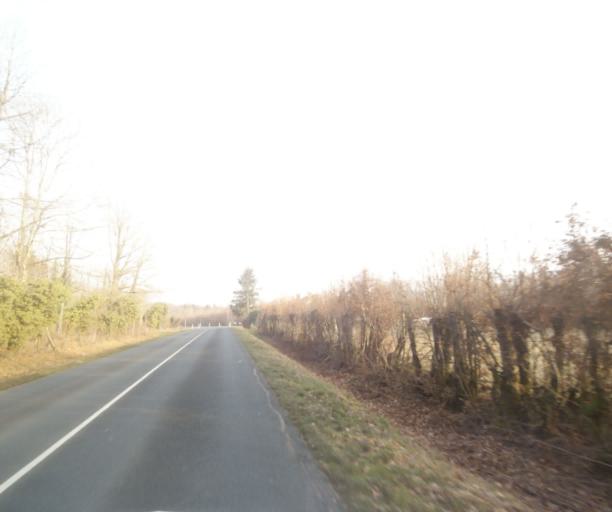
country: FR
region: Champagne-Ardenne
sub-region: Departement de la Haute-Marne
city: Chancenay
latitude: 48.6913
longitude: 4.9454
